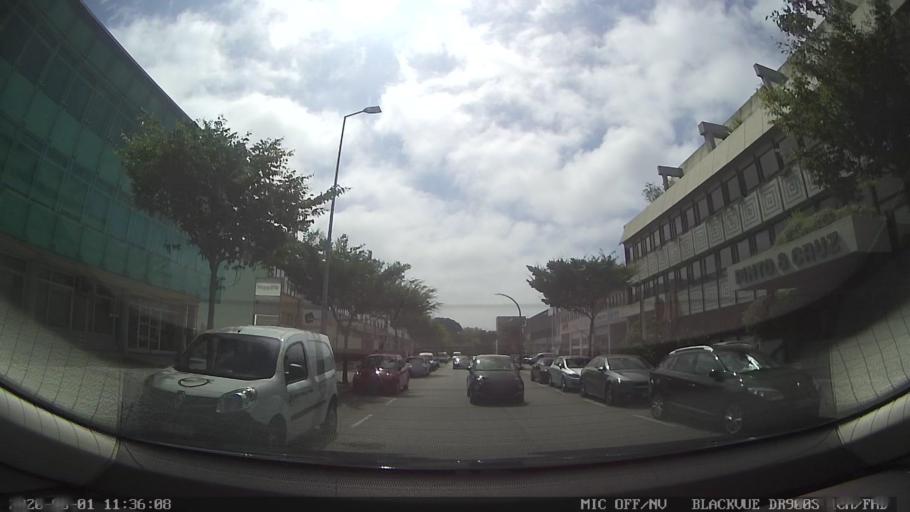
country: PT
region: Porto
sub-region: Matosinhos
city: Senhora da Hora
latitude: 41.1732
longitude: -8.6440
